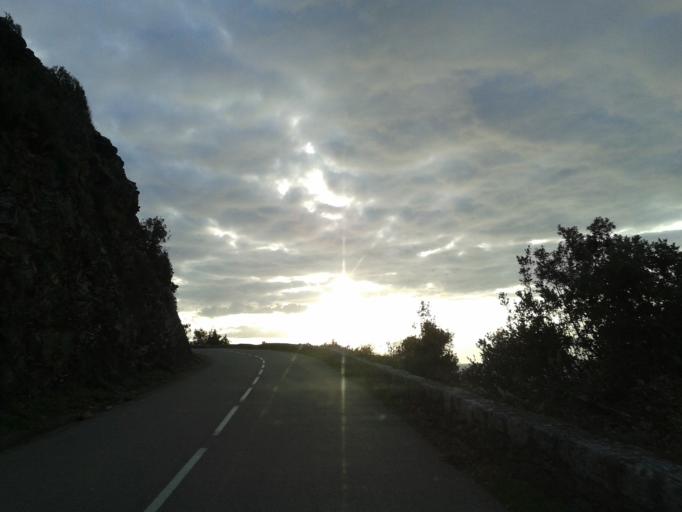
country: FR
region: Corsica
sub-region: Departement de la Haute-Corse
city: Saint-Florent
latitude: 42.7599
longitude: 9.3416
